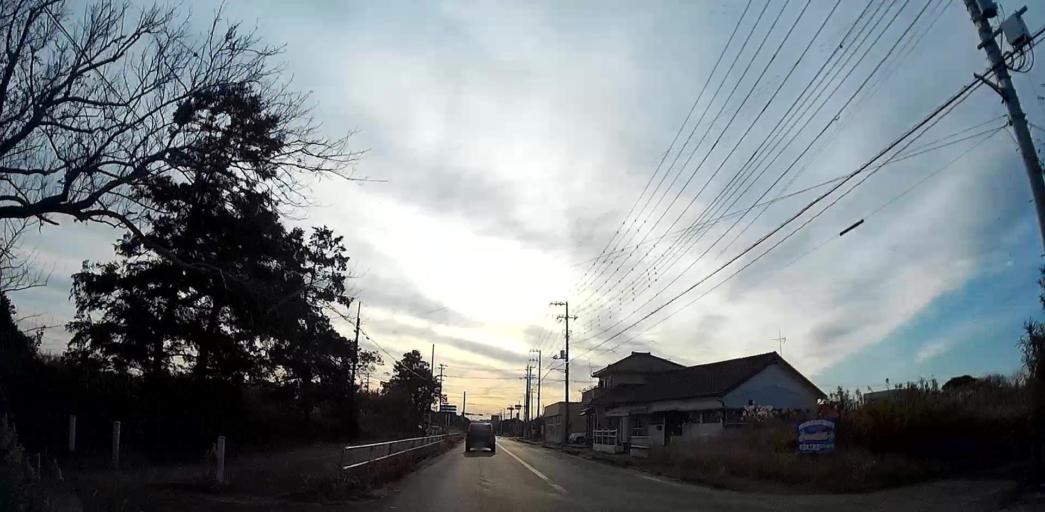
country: JP
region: Chiba
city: Hasaki
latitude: 35.7882
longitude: 140.7656
